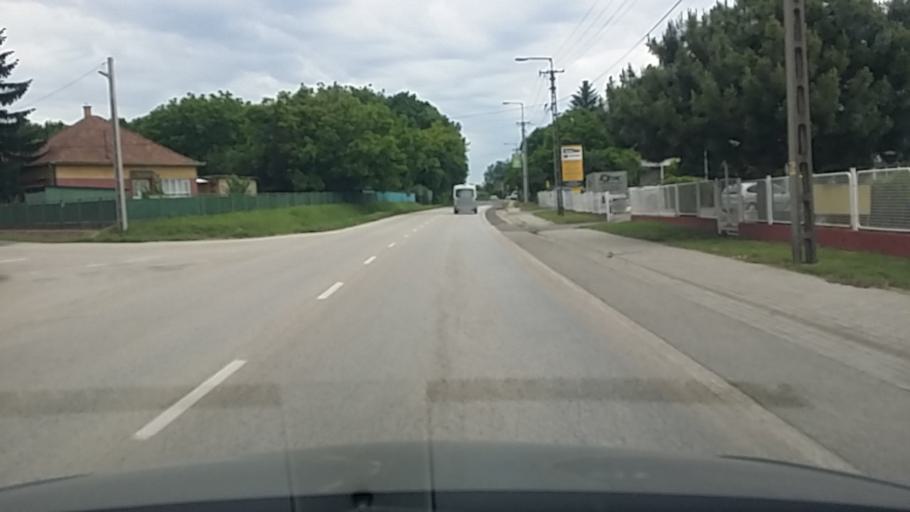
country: HU
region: Fejer
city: dunaujvaros
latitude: 46.9800
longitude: 18.9157
